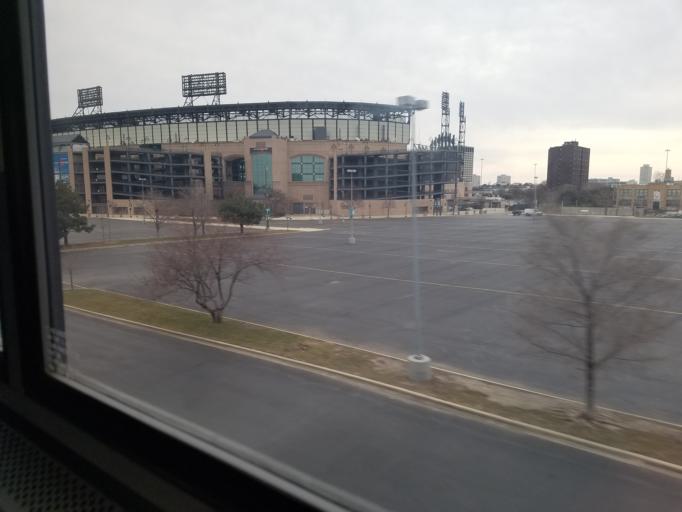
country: US
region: Illinois
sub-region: Cook County
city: Chicago
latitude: 41.8243
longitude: -87.6336
